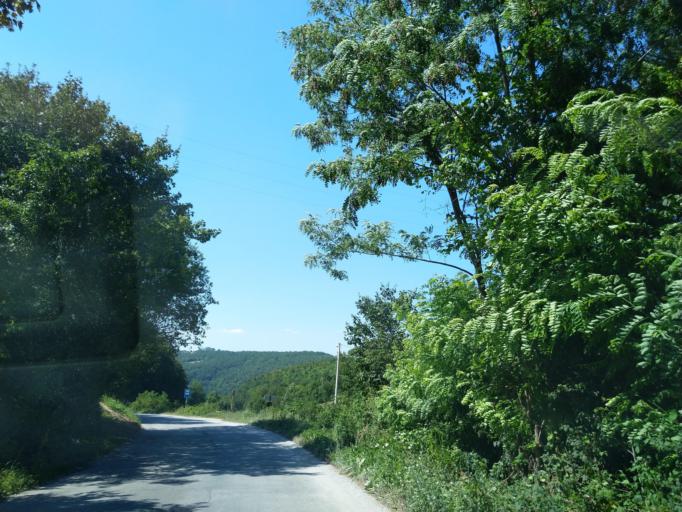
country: RS
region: Central Serbia
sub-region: Zlatiborski Okrug
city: Uzice
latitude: 43.8229
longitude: 19.8581
